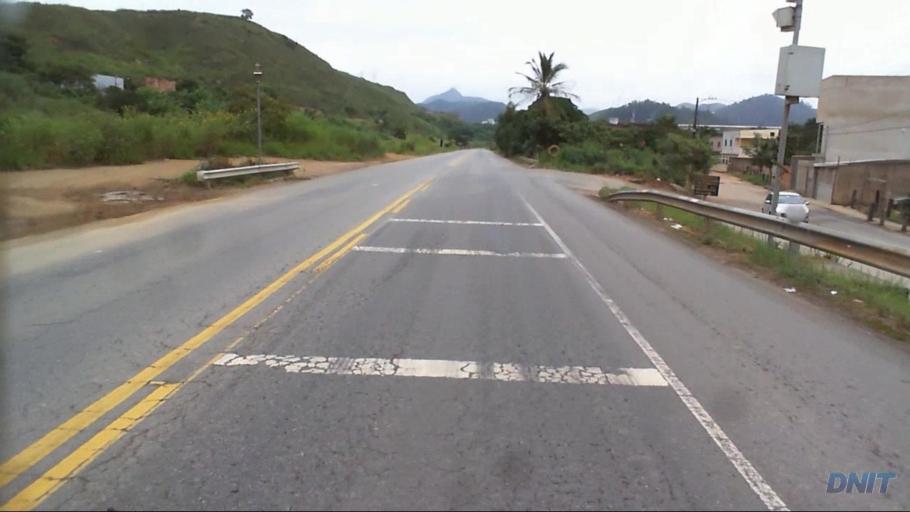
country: BR
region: Minas Gerais
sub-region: Coronel Fabriciano
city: Coronel Fabriciano
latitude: -19.5299
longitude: -42.6188
